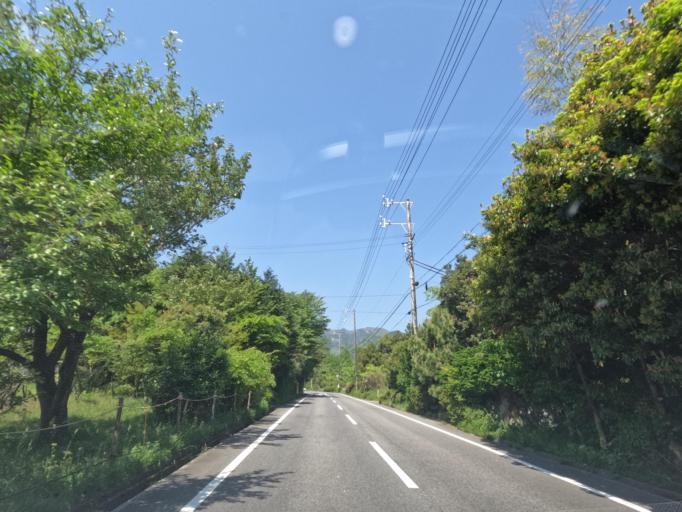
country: JP
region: Mie
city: Komono
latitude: 35.0228
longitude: 136.4762
